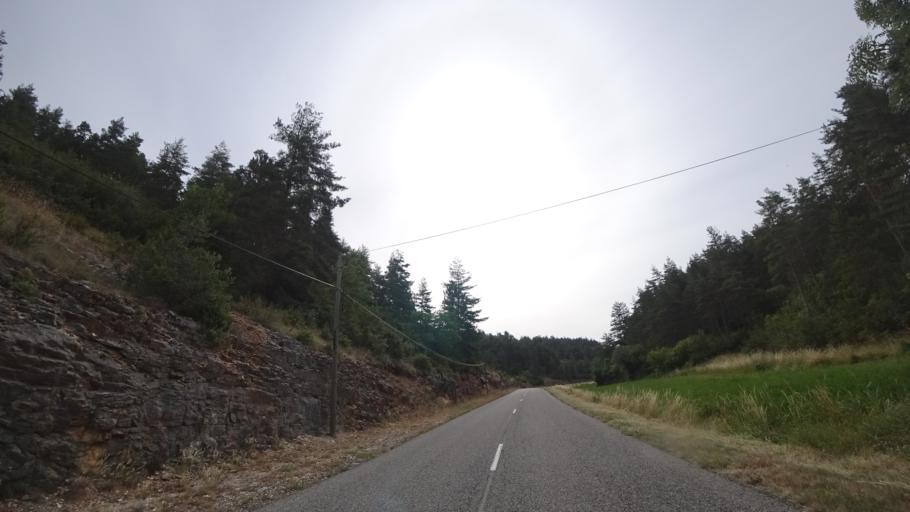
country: FR
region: Languedoc-Roussillon
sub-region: Departement de la Lozere
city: La Canourgue
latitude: 44.4105
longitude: 3.2720
